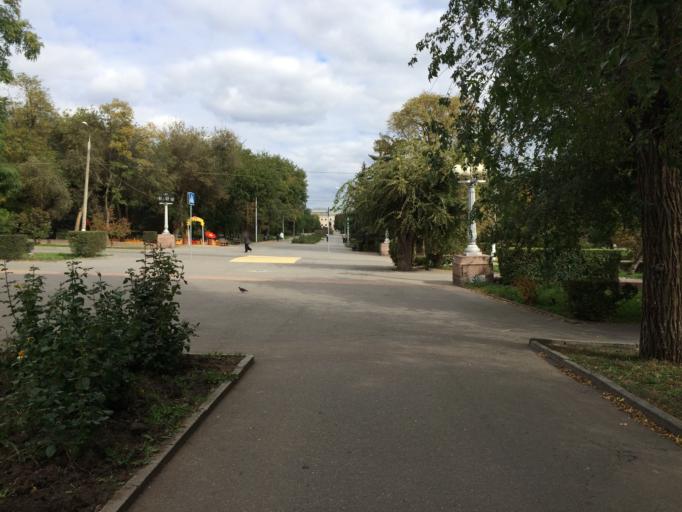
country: RU
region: Volgograd
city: Volgograd
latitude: 48.7023
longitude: 44.5166
